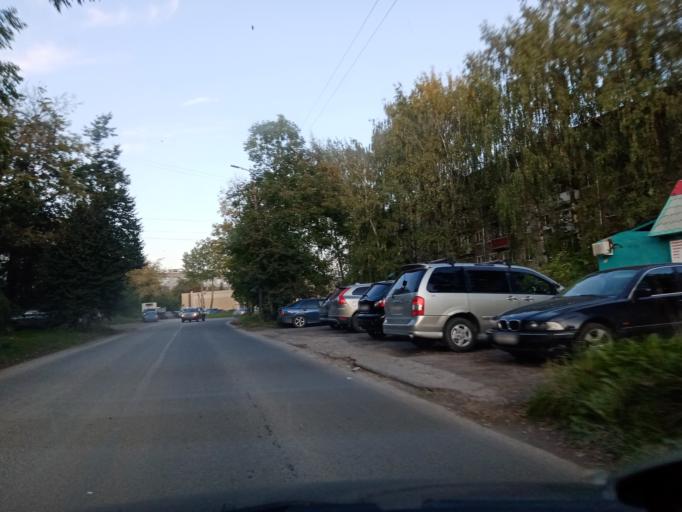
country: RU
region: Pskov
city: Pskov
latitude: 57.8059
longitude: 28.3422
